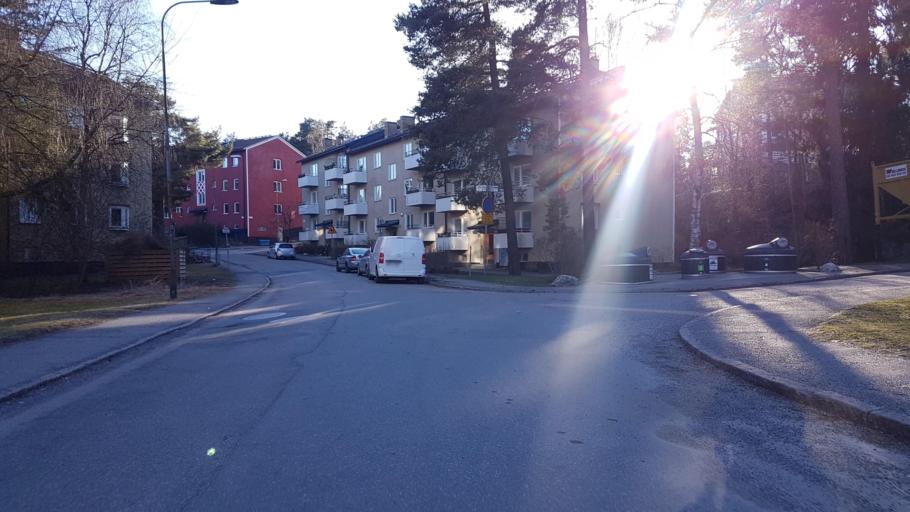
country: SE
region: Stockholm
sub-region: Stockholms Kommun
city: Arsta
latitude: 59.2662
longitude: 18.0771
